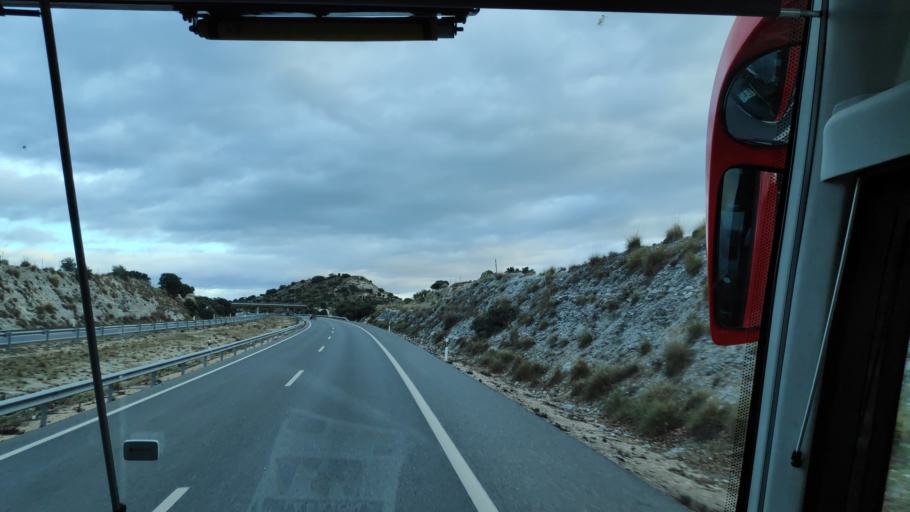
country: ES
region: Madrid
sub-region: Provincia de Madrid
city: Fuentiduena de Tajo
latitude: 40.1432
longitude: -3.2122
